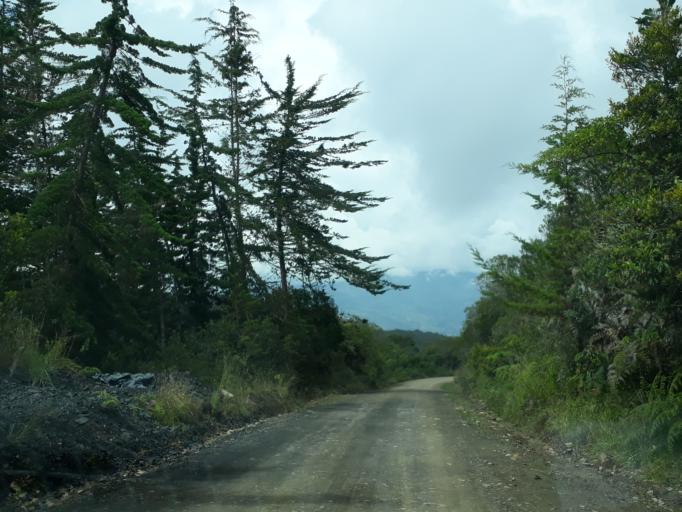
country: CO
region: Cundinamarca
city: Macheta
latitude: 5.1039
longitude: -73.5397
